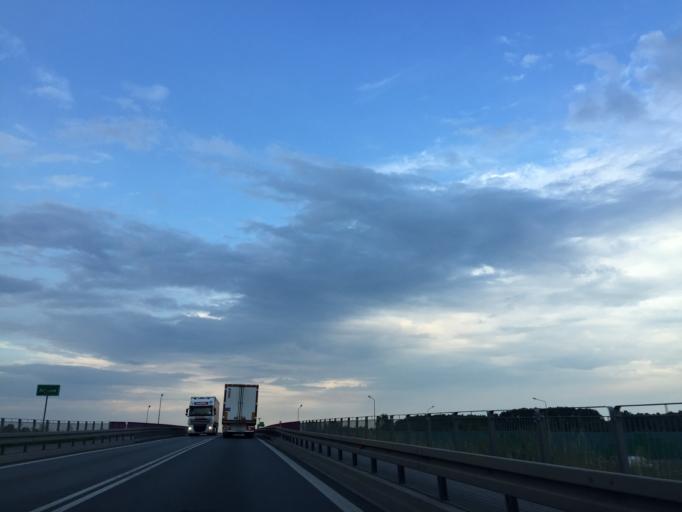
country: PL
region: Masovian Voivodeship
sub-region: Powiat minski
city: Minsk Mazowiecki
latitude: 52.2079
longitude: 21.5373
